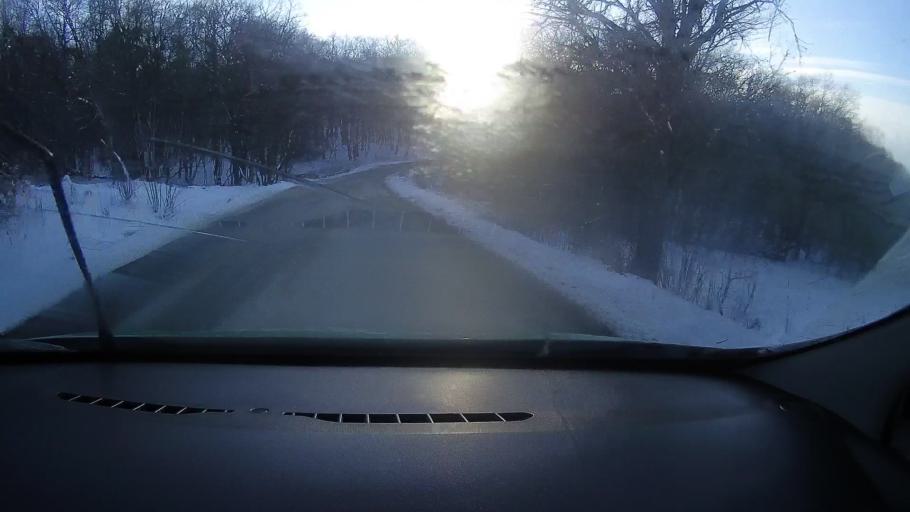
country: RO
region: Sibiu
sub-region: Oras Agnita
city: Ruja
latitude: 45.9875
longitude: 24.6780
